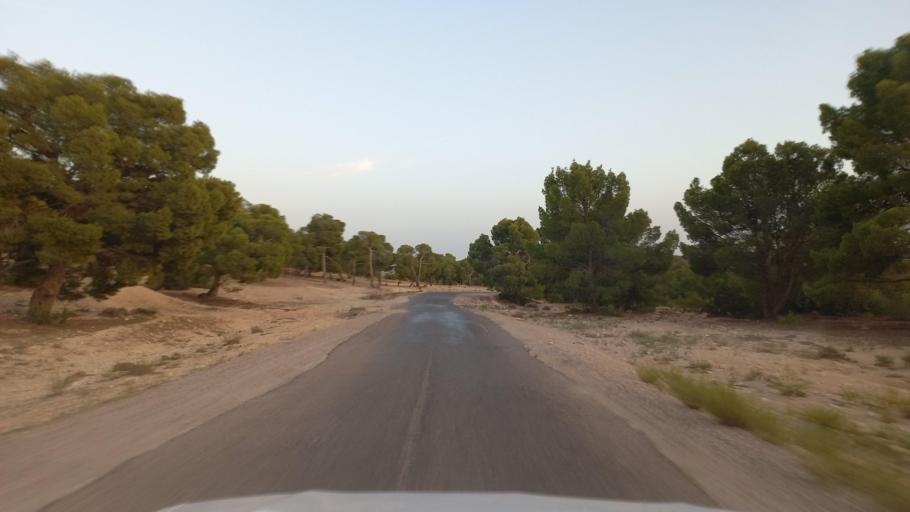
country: TN
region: Al Qasrayn
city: Sbiba
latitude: 35.4224
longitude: 8.9233
